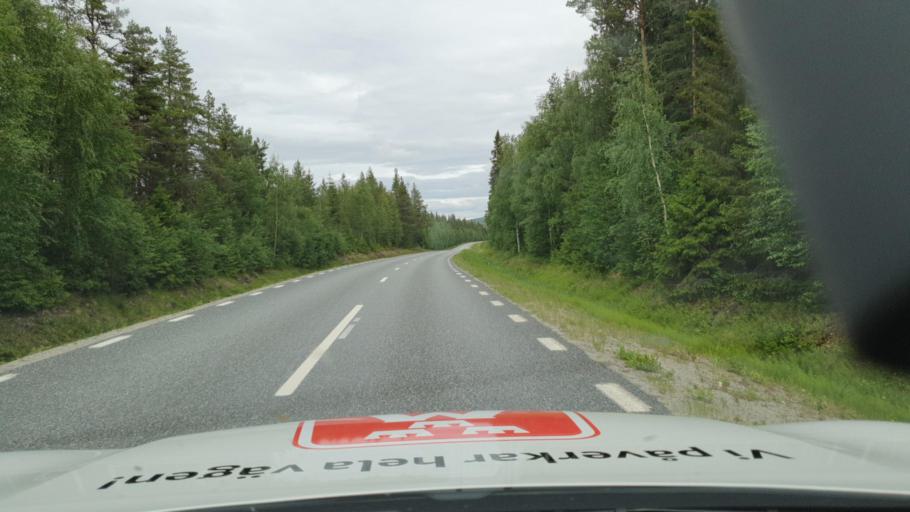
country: SE
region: Vaesterbotten
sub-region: Asele Kommun
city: Insjon
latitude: 64.2655
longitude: 17.5684
